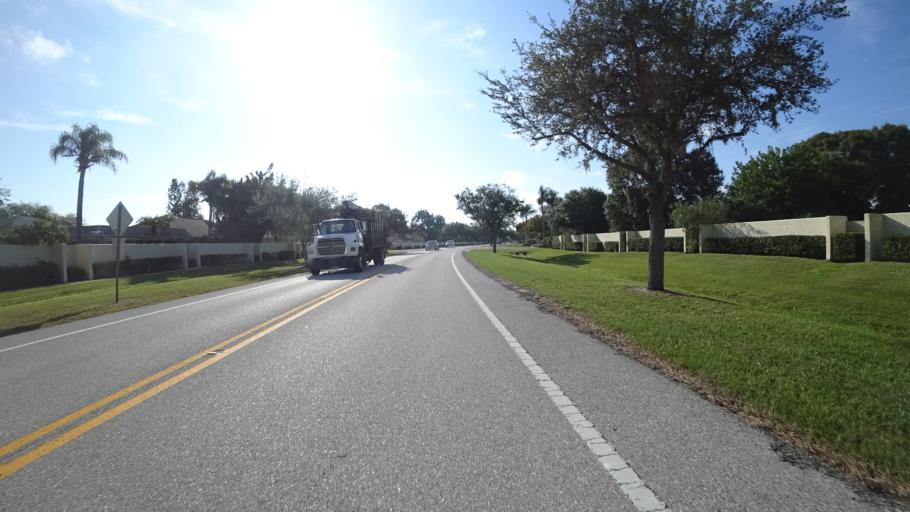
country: US
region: Florida
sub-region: Sarasota County
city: Desoto Lakes
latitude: 27.4176
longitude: -82.4925
